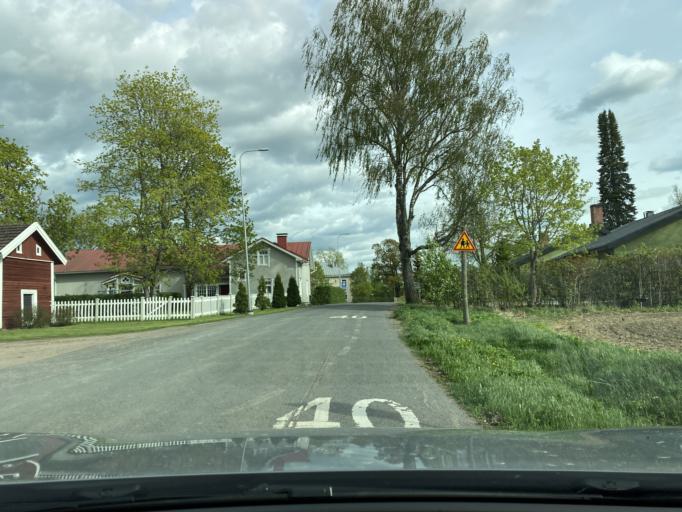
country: FI
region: Varsinais-Suomi
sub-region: Salo
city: Kiikala
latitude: 60.4620
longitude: 23.5507
